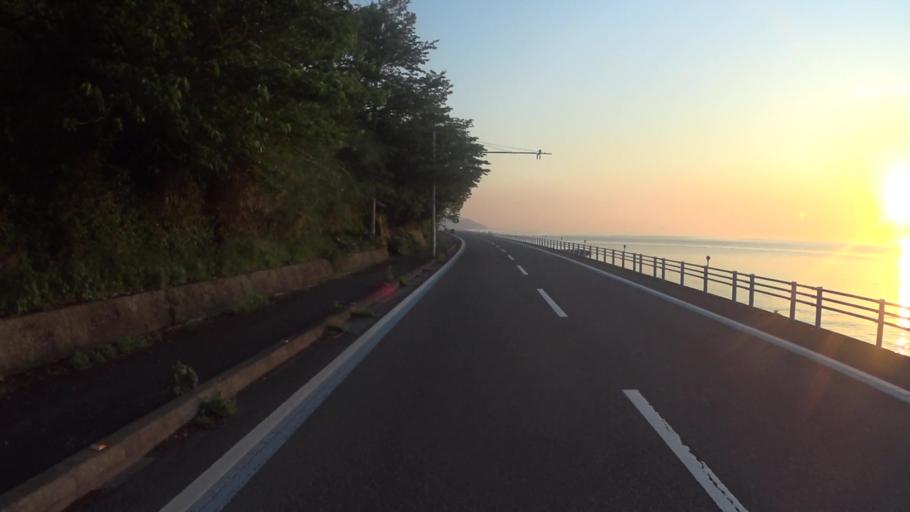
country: JP
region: Ehime
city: Iyo
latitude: 33.6748
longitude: 132.6159
